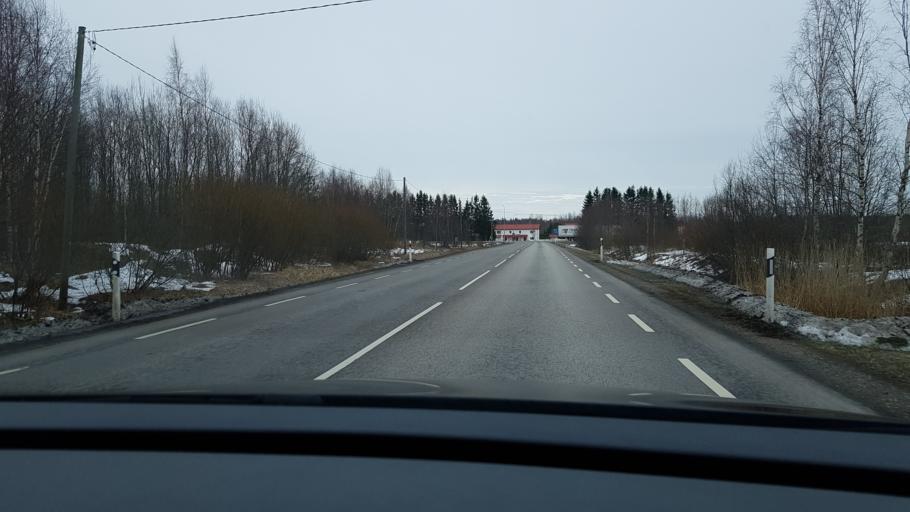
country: EE
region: Paernumaa
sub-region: Audru vald
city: Audru
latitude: 58.4030
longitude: 24.4299
